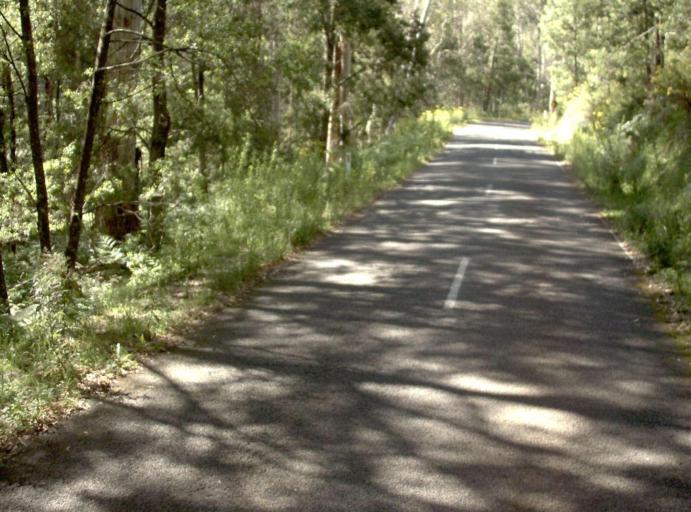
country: AU
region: New South Wales
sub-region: Bombala
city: Bombala
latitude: -37.3492
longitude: 148.6928
